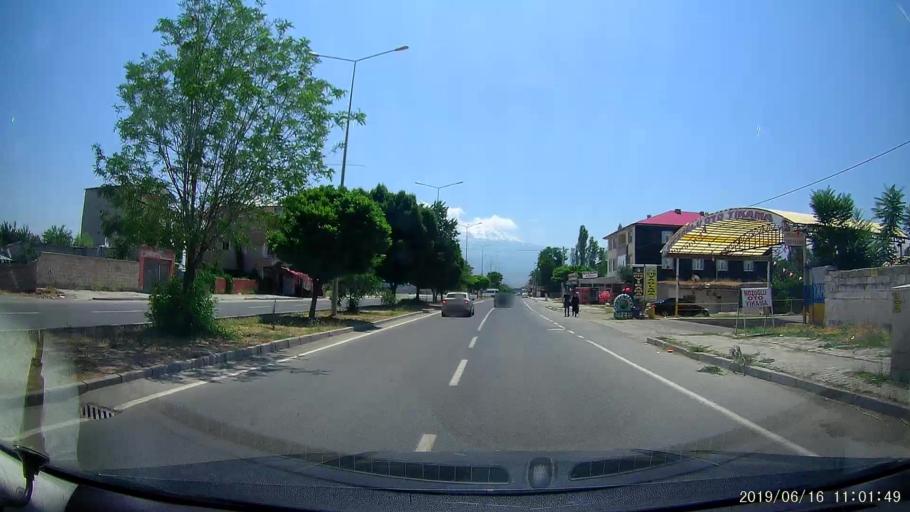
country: TR
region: Igdir
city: Igdir
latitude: 39.9123
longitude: 44.0538
